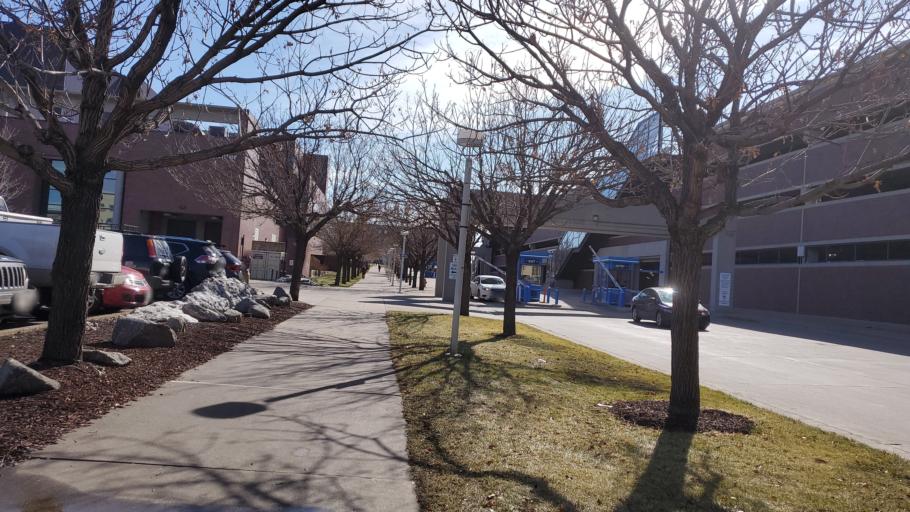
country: US
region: Colorado
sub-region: Denver County
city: Denver
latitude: 39.7443
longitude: -105.0073
